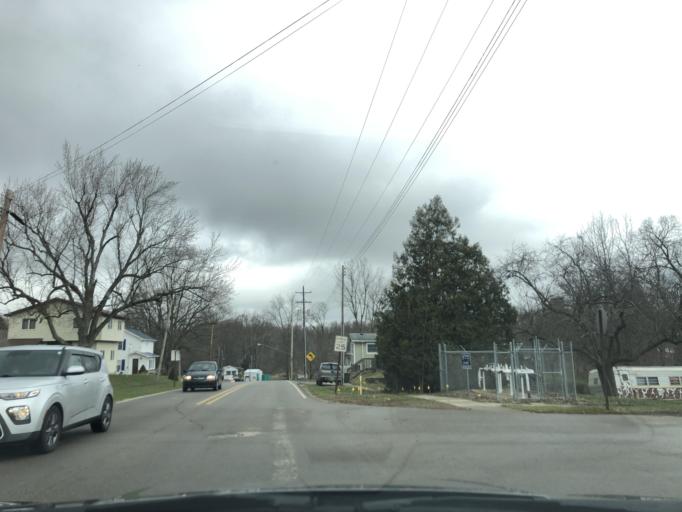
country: US
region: Michigan
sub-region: Clinton County
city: Fowler
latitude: 43.1055
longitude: -84.6922
